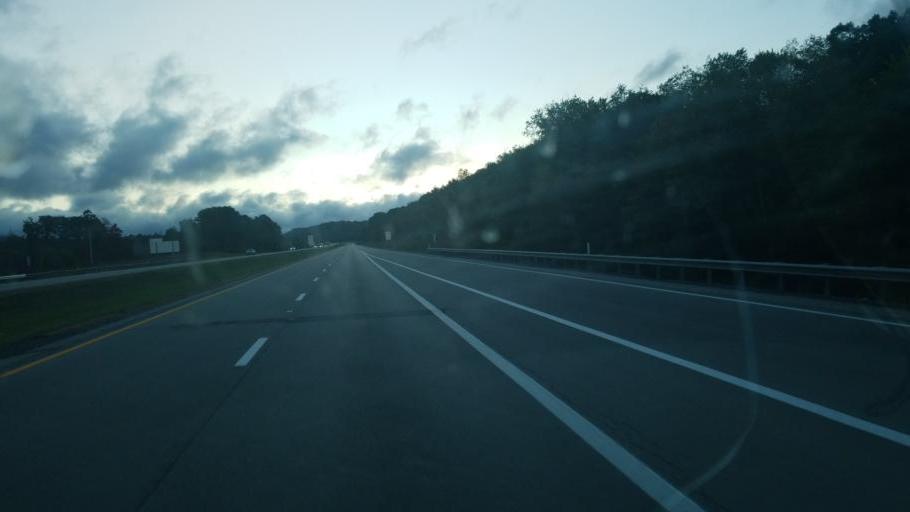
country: US
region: West Virginia
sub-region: Preston County
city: Terra Alta
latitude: 39.6578
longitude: -79.5292
